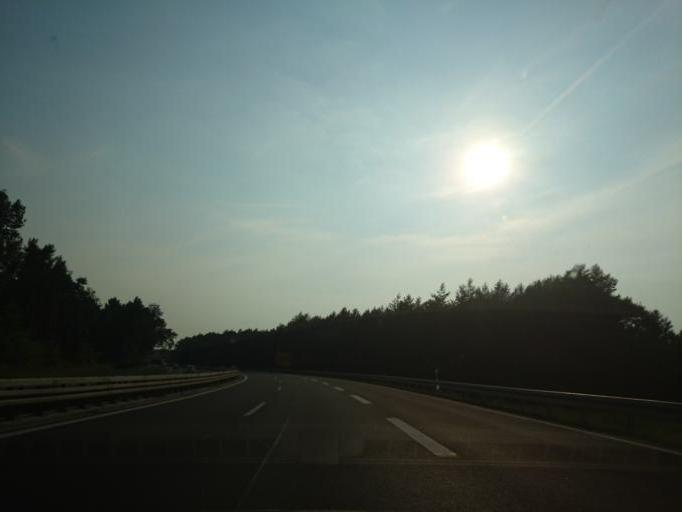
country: DE
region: Berlin
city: Wannsee
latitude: 52.3755
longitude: 13.1627
